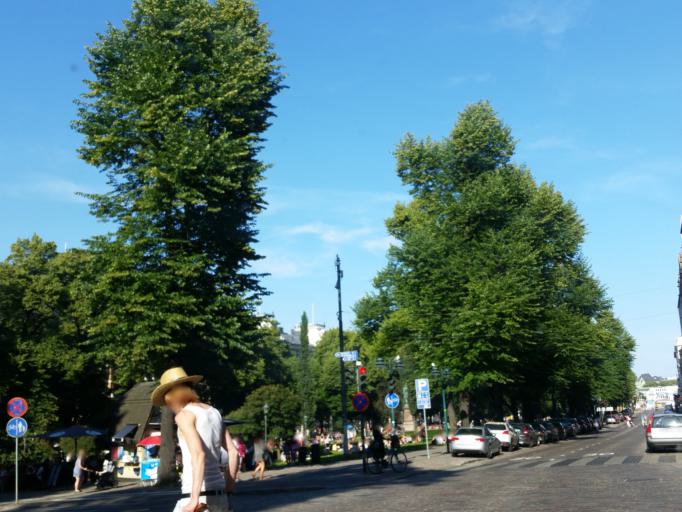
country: FI
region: Uusimaa
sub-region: Helsinki
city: Helsinki
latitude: 60.1671
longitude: 24.9454
